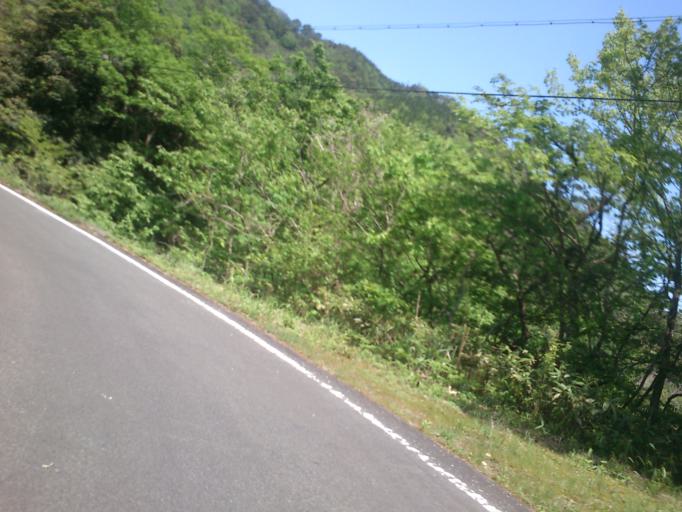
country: JP
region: Kyoto
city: Miyazu
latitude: 35.6998
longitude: 135.1568
